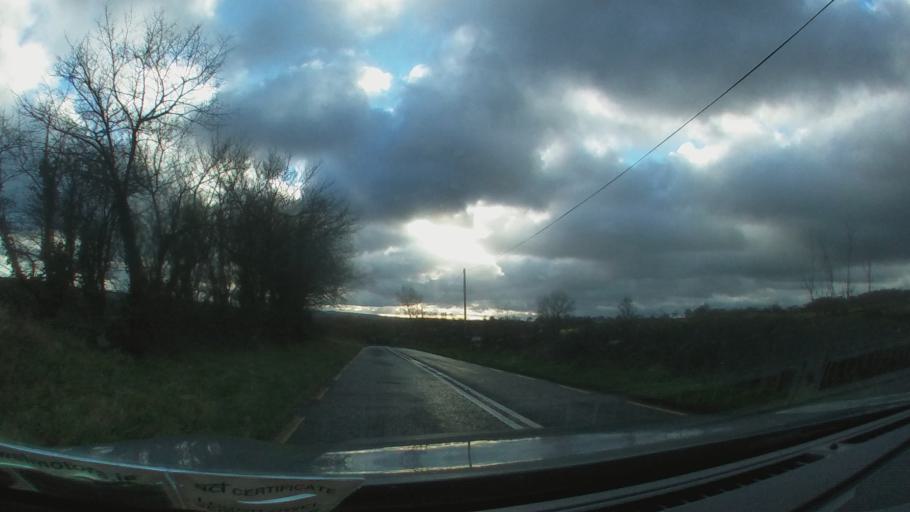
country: IE
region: Leinster
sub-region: Kilkenny
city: Thomastown
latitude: 52.5635
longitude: -7.1199
